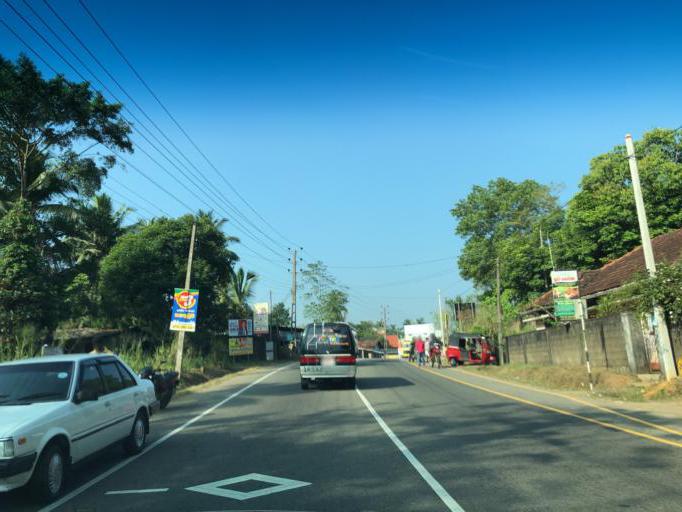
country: LK
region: Western
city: Horana South
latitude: 6.7239
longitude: 80.0840
